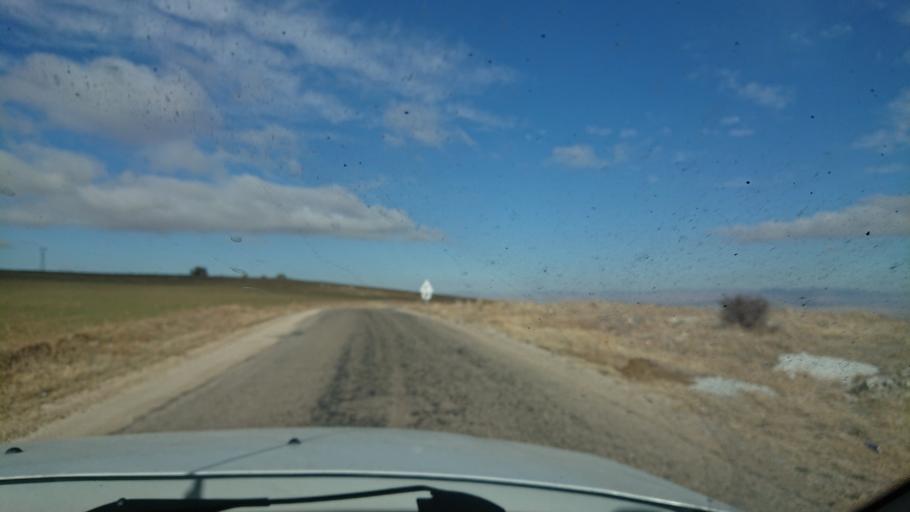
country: TR
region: Aksaray
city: Agacoren
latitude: 38.8393
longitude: 33.9532
